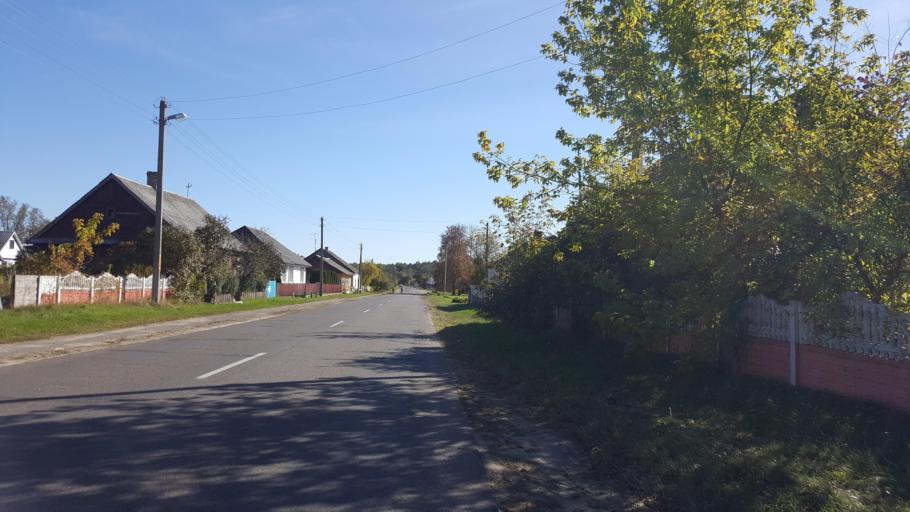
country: BY
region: Brest
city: Kamyanyets
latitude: 52.4046
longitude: 23.7903
